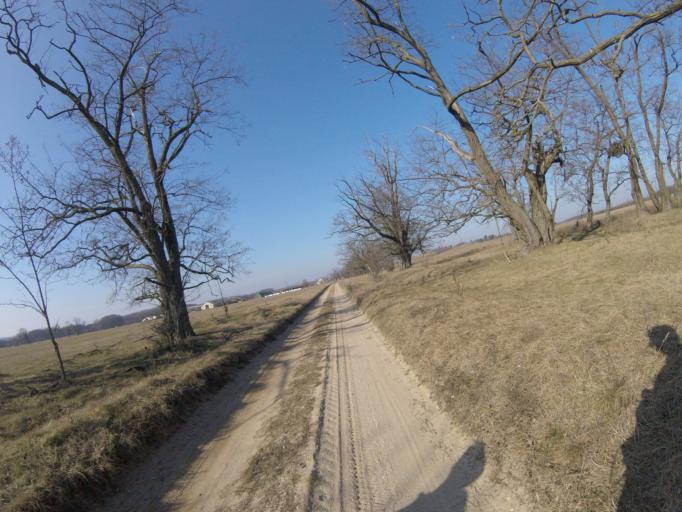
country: HU
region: Komarom-Esztergom
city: Oroszlany
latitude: 47.4683
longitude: 18.3388
